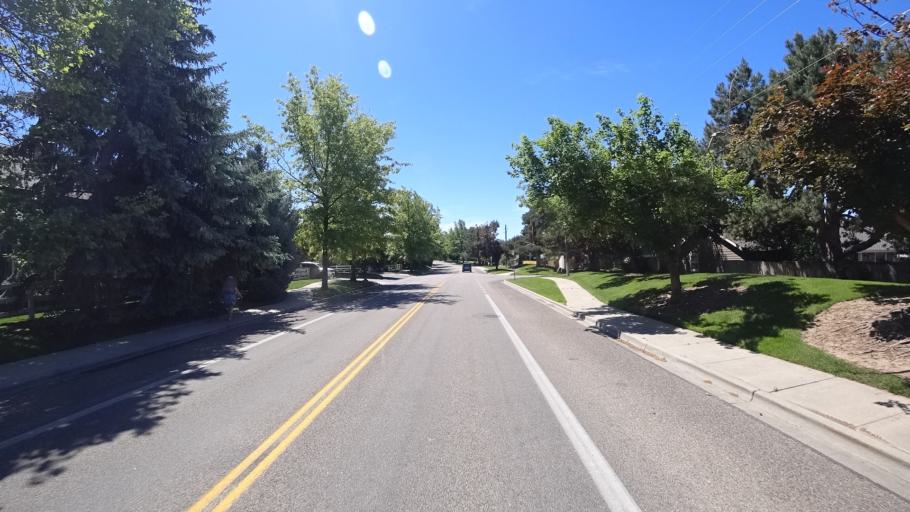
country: US
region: Idaho
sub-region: Ada County
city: Boise
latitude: 43.5725
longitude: -116.1836
